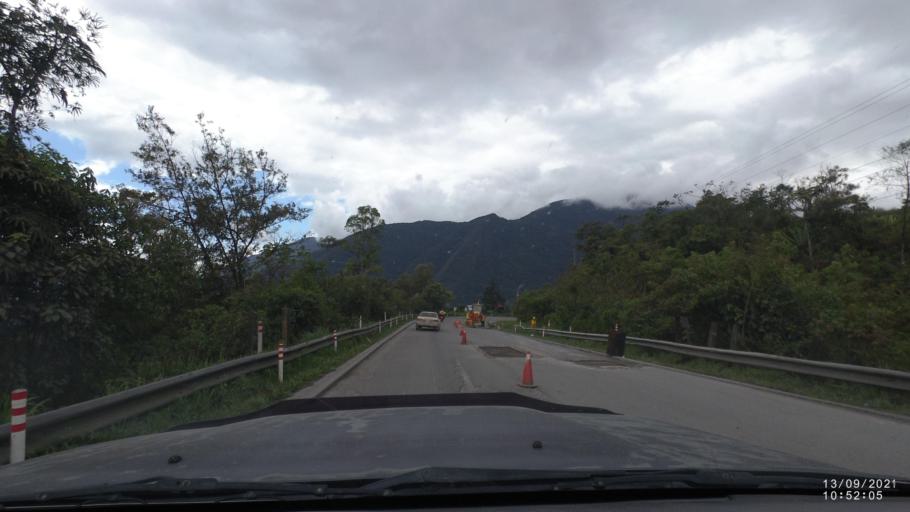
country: BO
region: Cochabamba
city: Colomi
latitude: -17.1989
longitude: -65.8389
